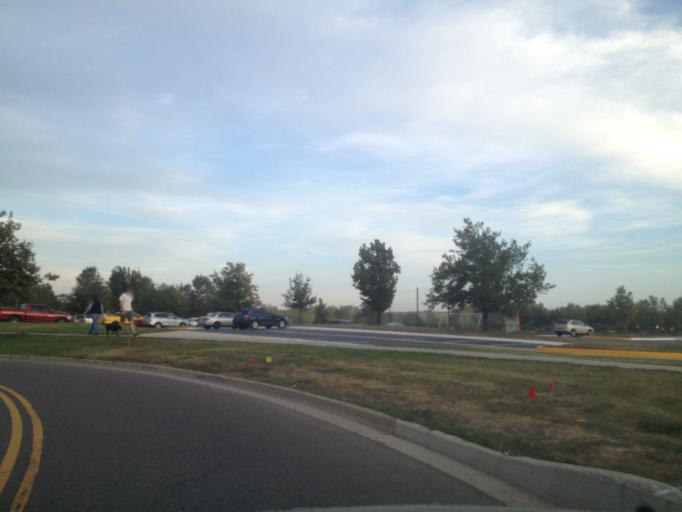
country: US
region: Colorado
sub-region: Boulder County
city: Boulder
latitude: 39.9931
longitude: -105.2243
